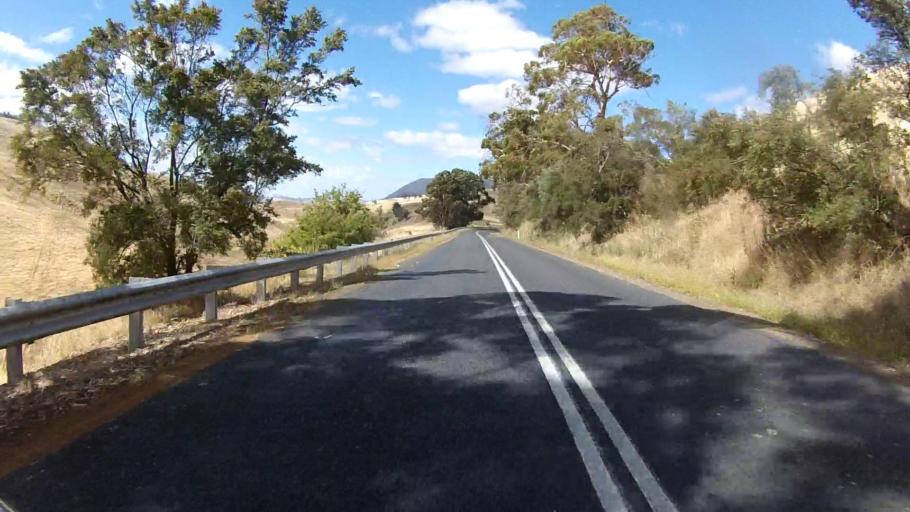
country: AU
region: Tasmania
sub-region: Brighton
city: Bridgewater
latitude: -42.5630
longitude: 147.3912
